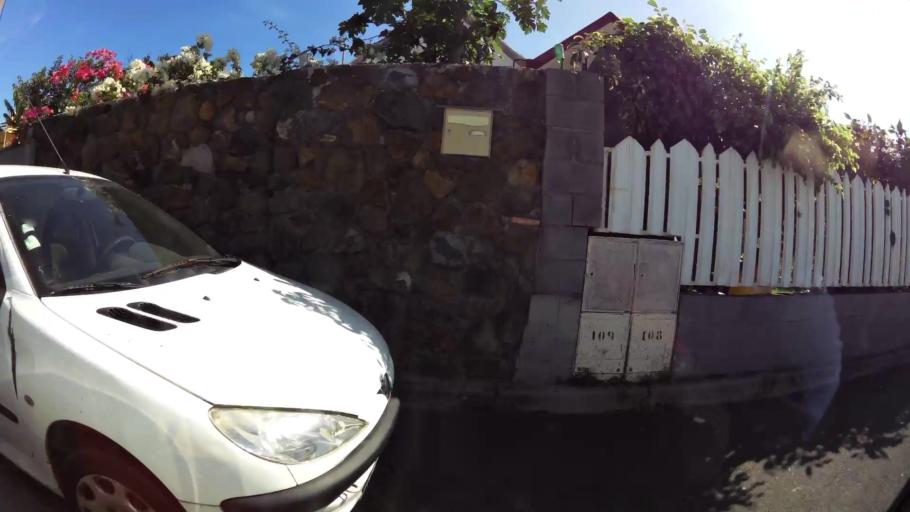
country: RE
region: Reunion
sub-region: Reunion
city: Saint-Pierre
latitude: -21.3368
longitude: 55.4607
